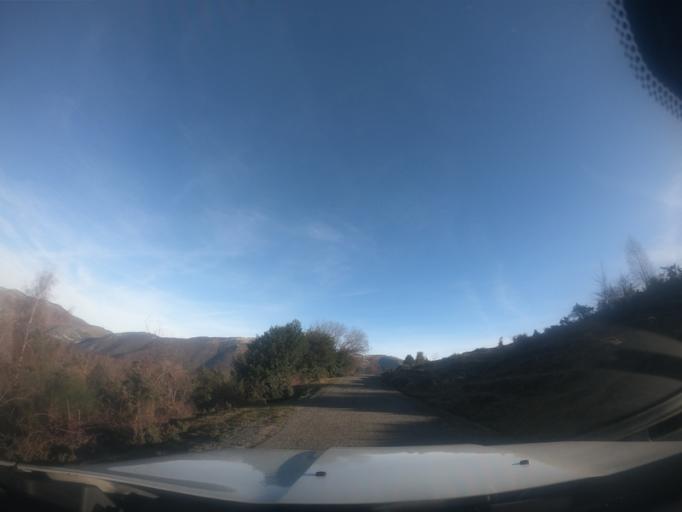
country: FR
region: Midi-Pyrenees
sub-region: Departement des Hautes-Pyrenees
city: Campan
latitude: 42.9451
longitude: 0.2348
